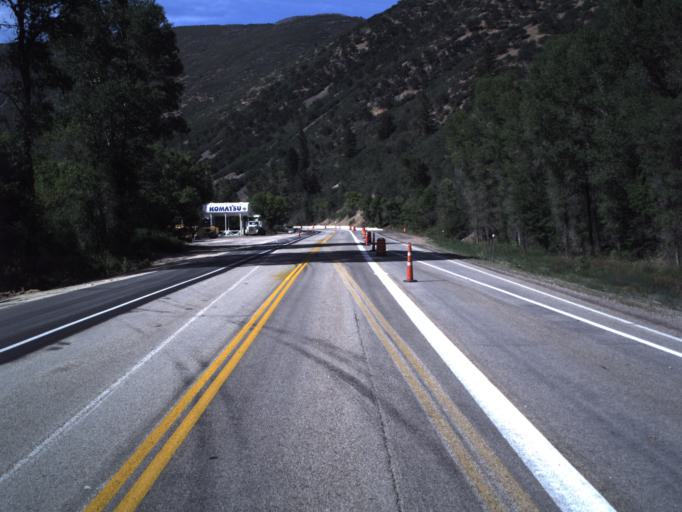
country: US
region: Utah
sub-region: Wasatch County
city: Heber
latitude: 40.3914
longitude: -111.3027
